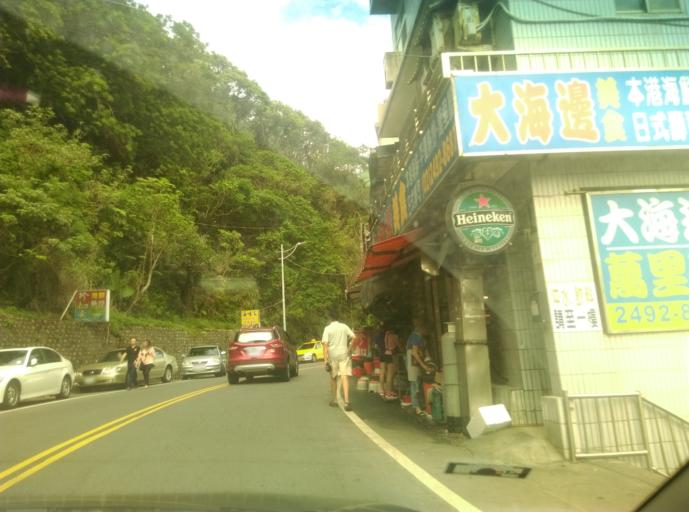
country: TW
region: Taiwan
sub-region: Keelung
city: Keelung
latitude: 25.1936
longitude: 121.6857
